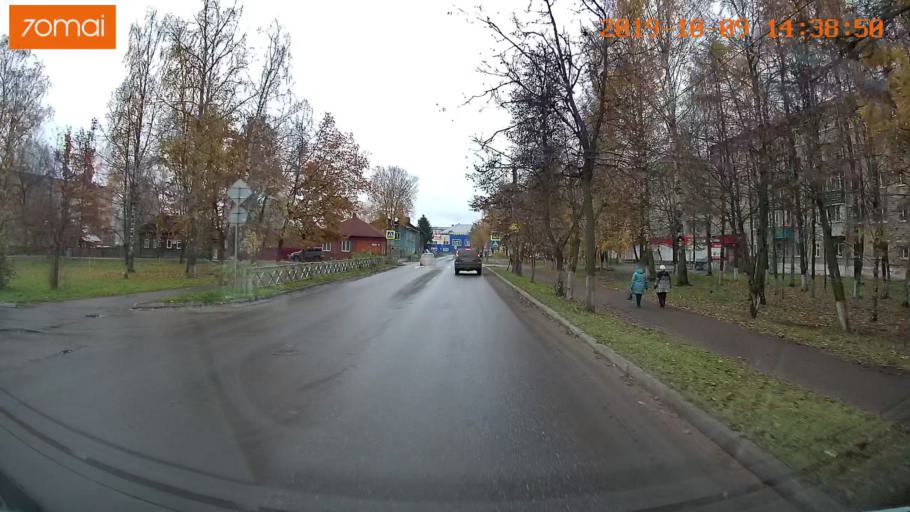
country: RU
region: Kostroma
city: Buy
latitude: 58.4784
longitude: 41.5372
